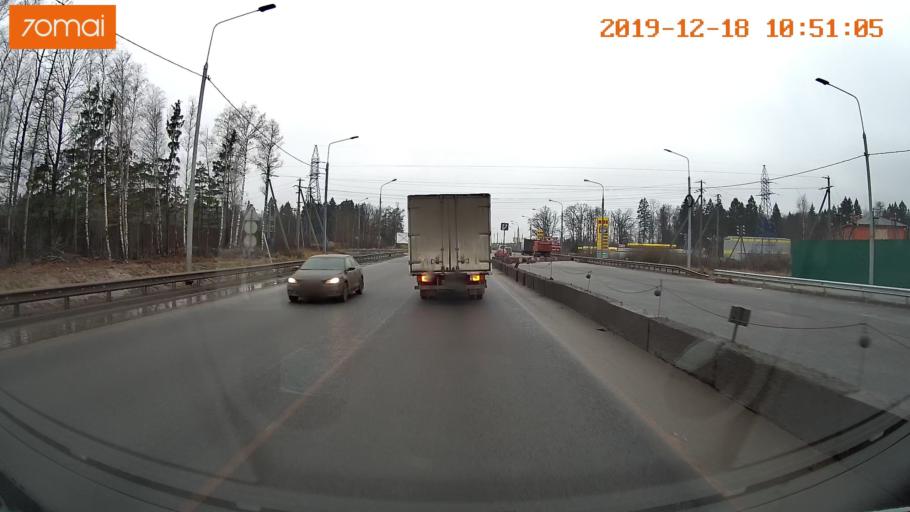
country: RU
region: Moskovskaya
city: Selyatino
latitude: 55.5128
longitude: 37.0007
